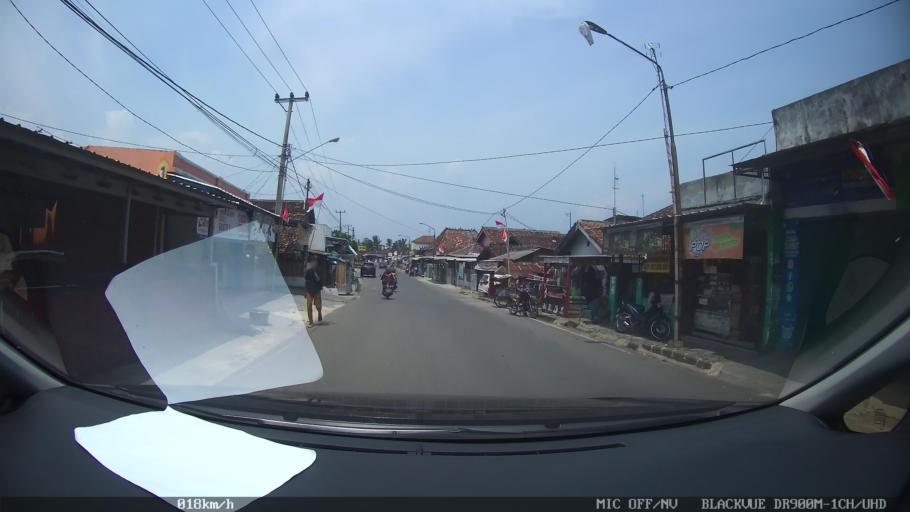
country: ID
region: Lampung
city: Bandarlampung
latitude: -5.4464
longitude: 105.2517
